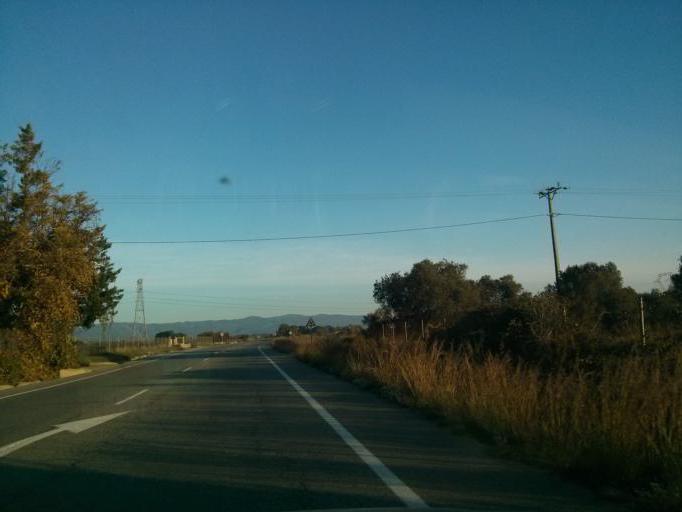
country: ES
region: Catalonia
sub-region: Provincia de Tarragona
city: Santa Oliva
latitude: 41.2442
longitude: 1.5455
